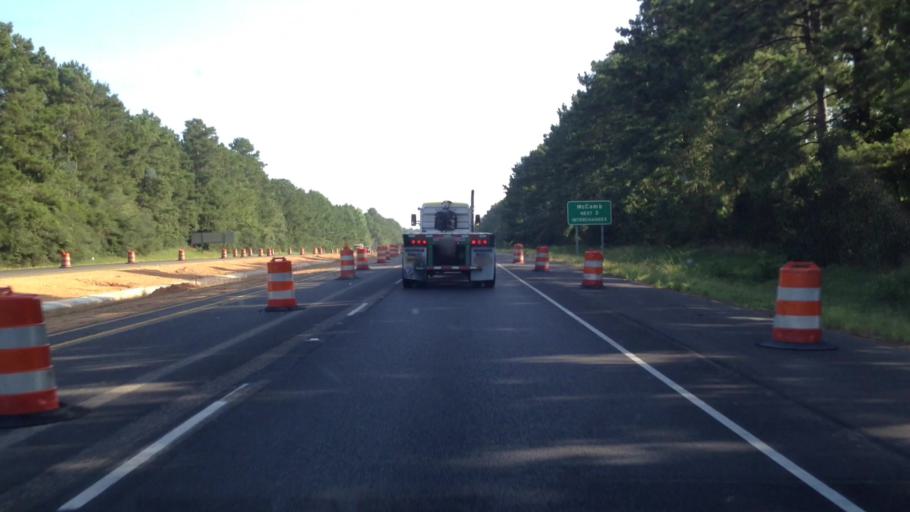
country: US
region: Mississippi
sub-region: Pike County
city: McComb
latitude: 31.1993
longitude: -90.4840
